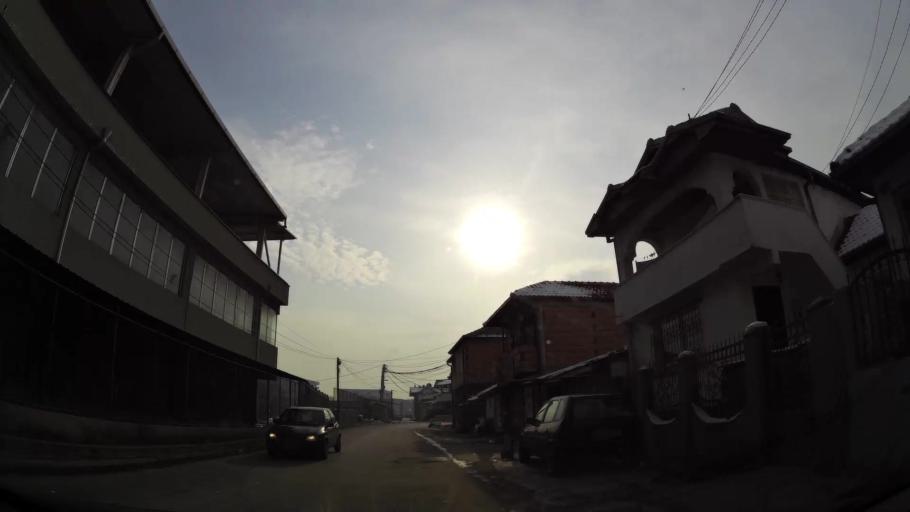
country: MK
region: Cair
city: Cair
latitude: 42.0120
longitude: 21.4316
